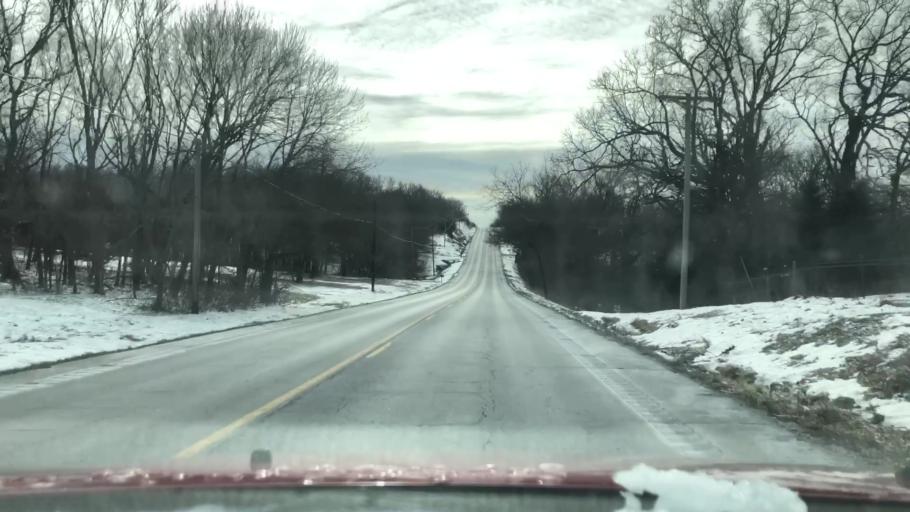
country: US
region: Missouri
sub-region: Jackson County
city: Oak Grove
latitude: 38.9727
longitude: -94.1307
